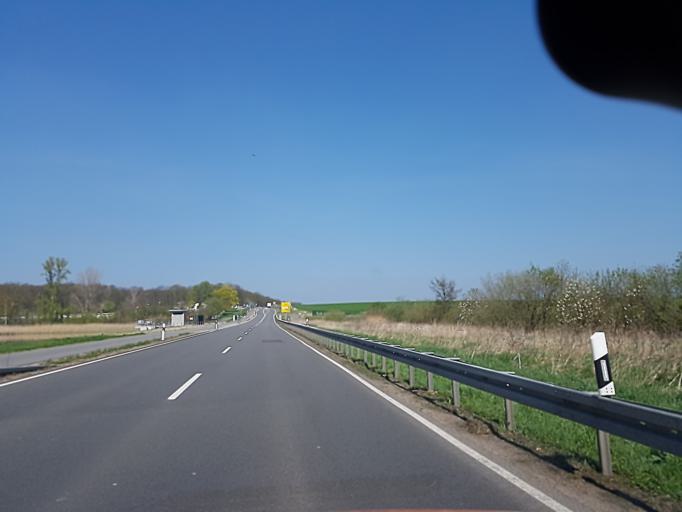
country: DE
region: Saxony
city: Mutzschen
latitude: 51.2630
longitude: 12.9193
